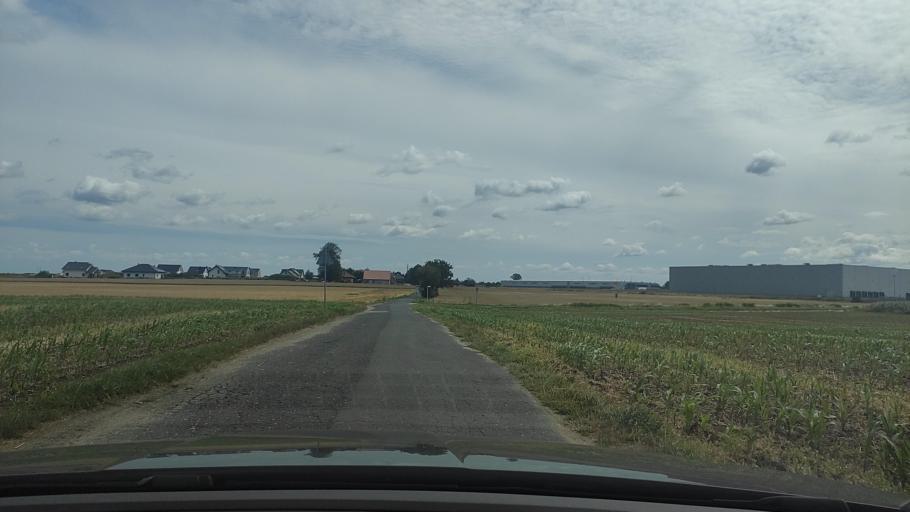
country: PL
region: Greater Poland Voivodeship
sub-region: Powiat poznanski
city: Kostrzyn
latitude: 52.4063
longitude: 17.1985
